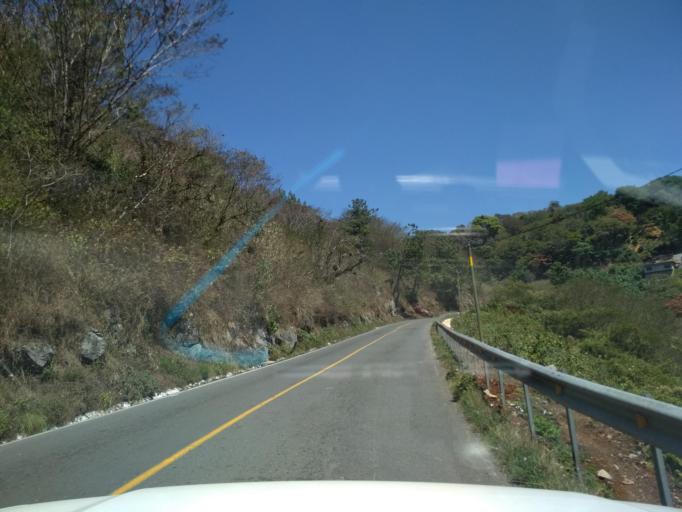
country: MX
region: Veracruz
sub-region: Tlilapan
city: Tonalixco
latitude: 18.7739
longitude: -97.0829
